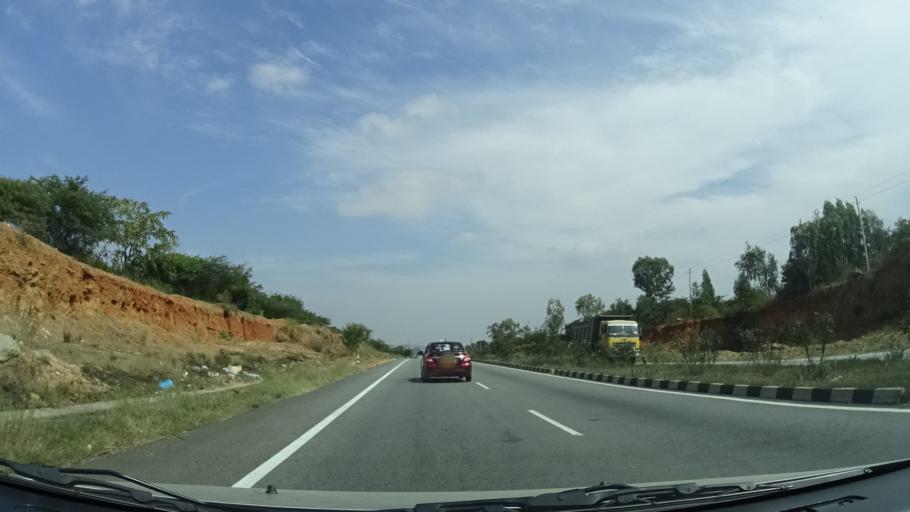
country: IN
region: Karnataka
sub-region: Chikkaballapur
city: Chik Ballapur
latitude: 13.5553
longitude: 77.7776
